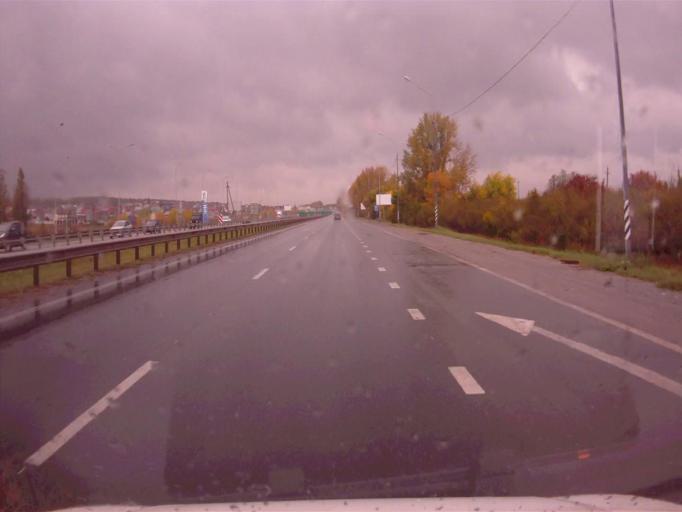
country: RU
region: Chelyabinsk
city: Dolgoderevenskoye
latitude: 55.2761
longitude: 61.3438
